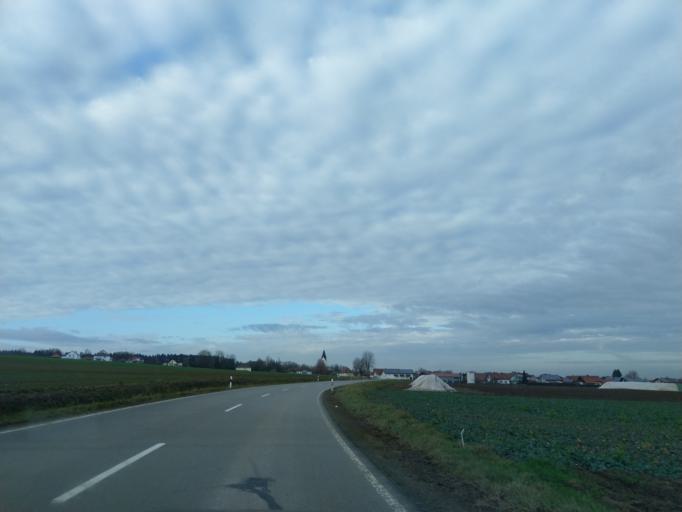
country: DE
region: Bavaria
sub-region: Lower Bavaria
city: Wallerfing
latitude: 48.6836
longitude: 12.8888
